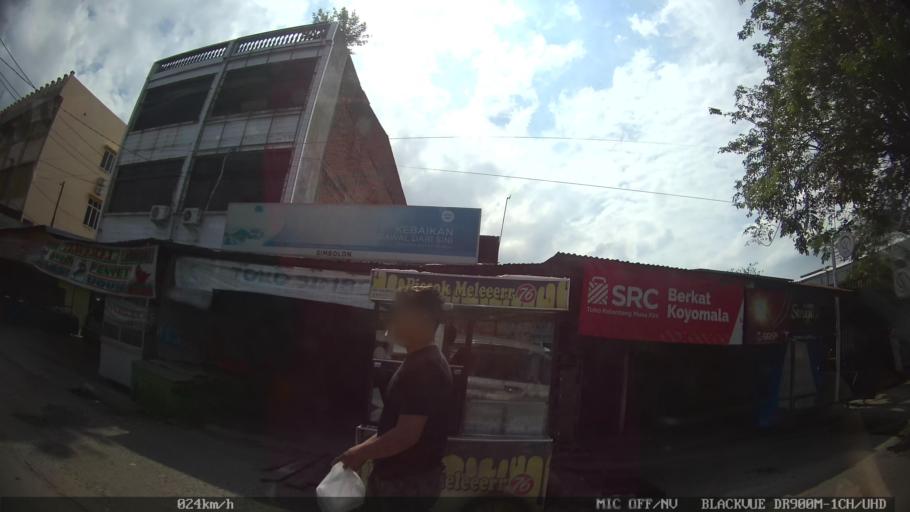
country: ID
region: North Sumatra
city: Medan
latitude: 3.6081
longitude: 98.6450
